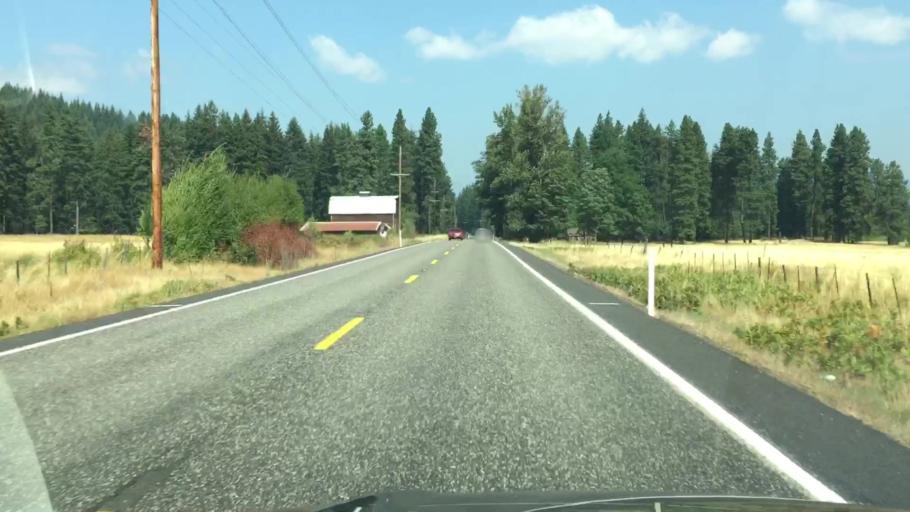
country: US
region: Washington
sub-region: Klickitat County
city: White Salmon
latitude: 45.9541
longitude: -121.4899
